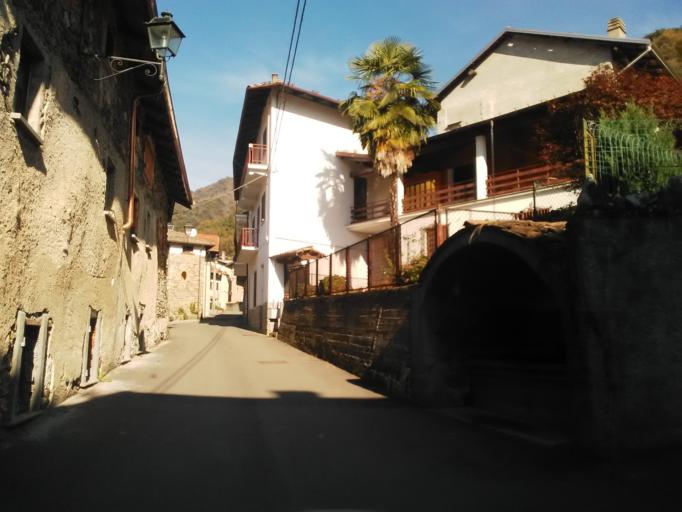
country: IT
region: Piedmont
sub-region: Provincia di Vercelli
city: Postua
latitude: 45.7211
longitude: 8.2210
